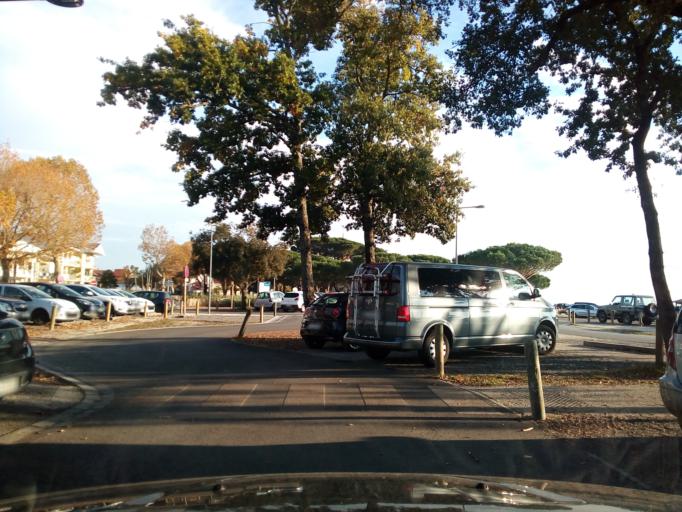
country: FR
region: Aquitaine
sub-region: Departement de la Gironde
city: Andernos-les-Bains
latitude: 44.7441
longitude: -1.1069
